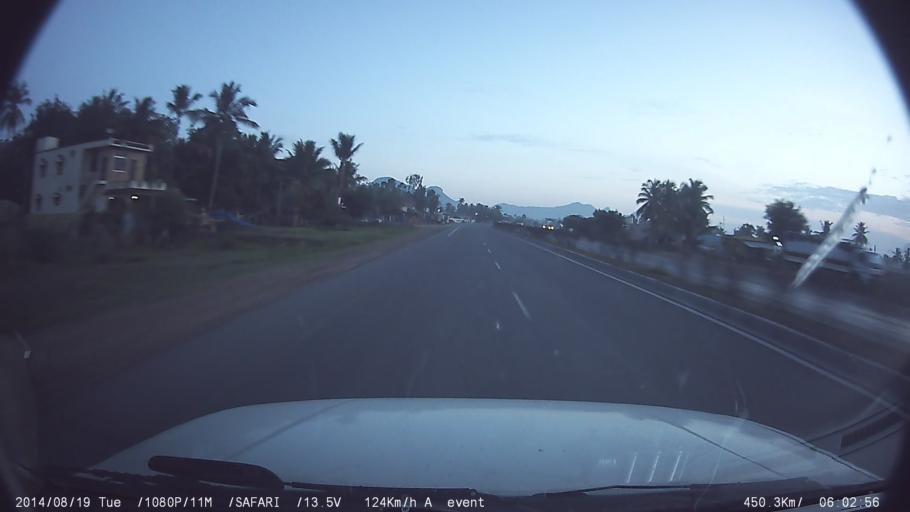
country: IN
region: Tamil Nadu
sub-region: Salem
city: Omalur
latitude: 11.8463
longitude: 78.0680
